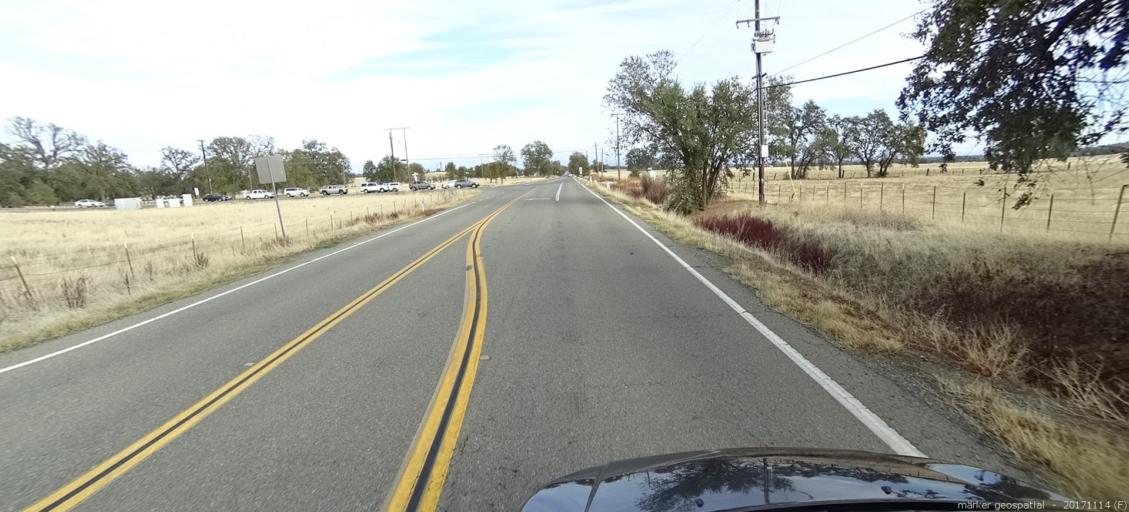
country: US
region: California
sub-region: Shasta County
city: Anderson
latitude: 40.3886
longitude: -122.4081
